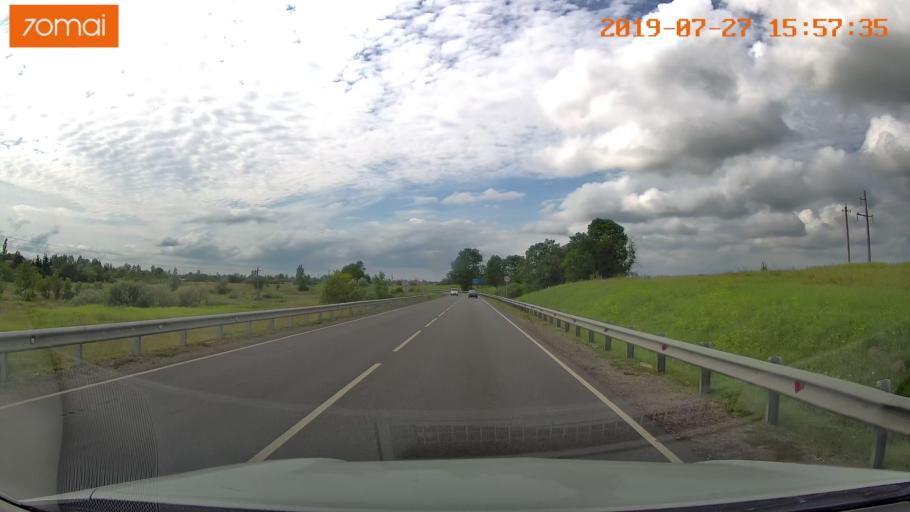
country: RU
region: Kaliningrad
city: Chernyakhovsk
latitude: 54.6242
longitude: 21.8813
